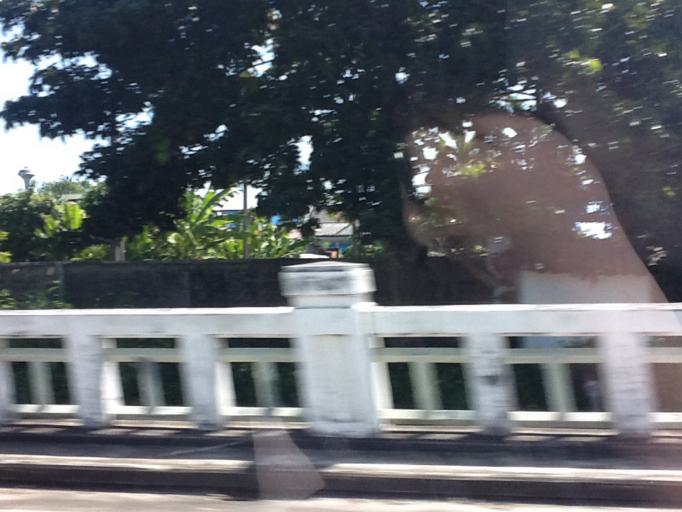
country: TH
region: Phuket
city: Ban Ko Kaeo
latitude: 7.9555
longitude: 98.3853
